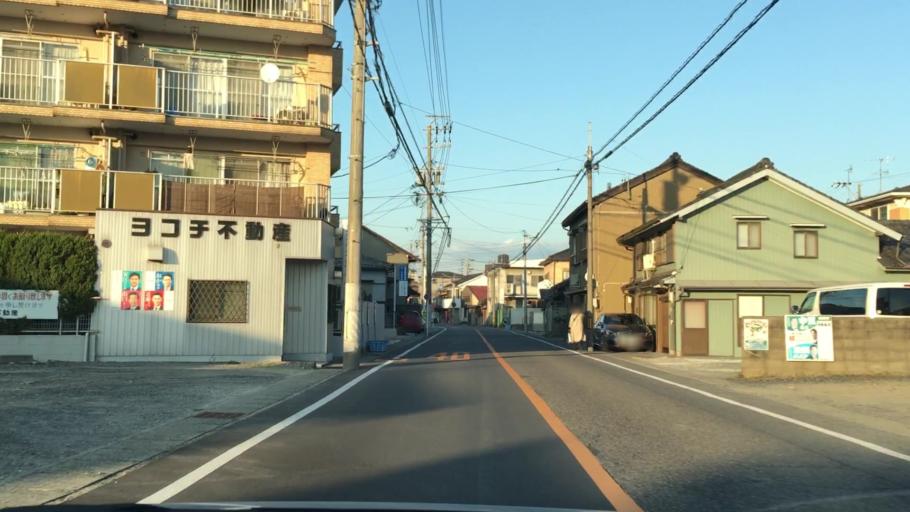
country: JP
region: Aichi
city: Obu
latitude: 35.0728
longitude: 136.9428
